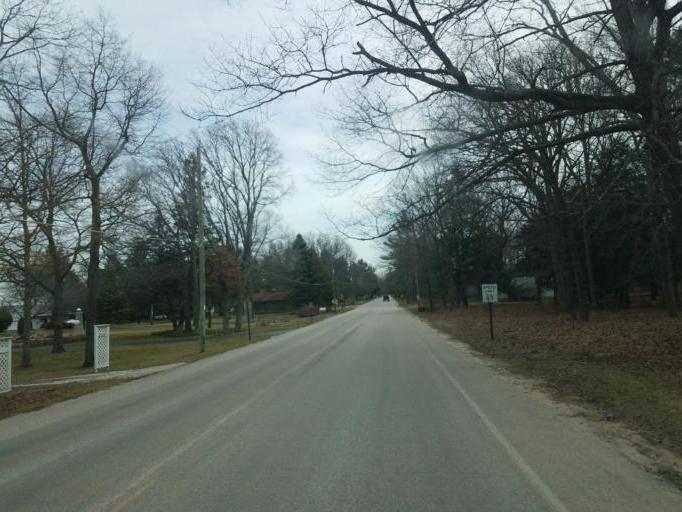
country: US
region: Michigan
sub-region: Oceana County
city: Hart
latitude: 43.6586
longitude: -86.5125
